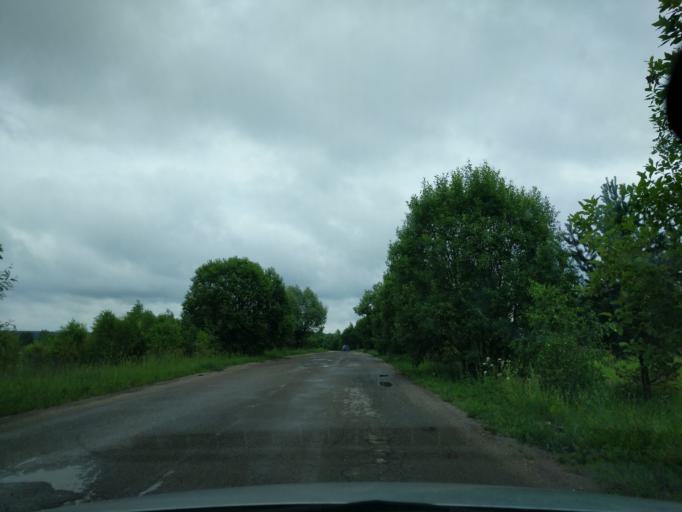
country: RU
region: Kaluga
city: Myatlevo
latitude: 54.8562
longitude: 35.5801
